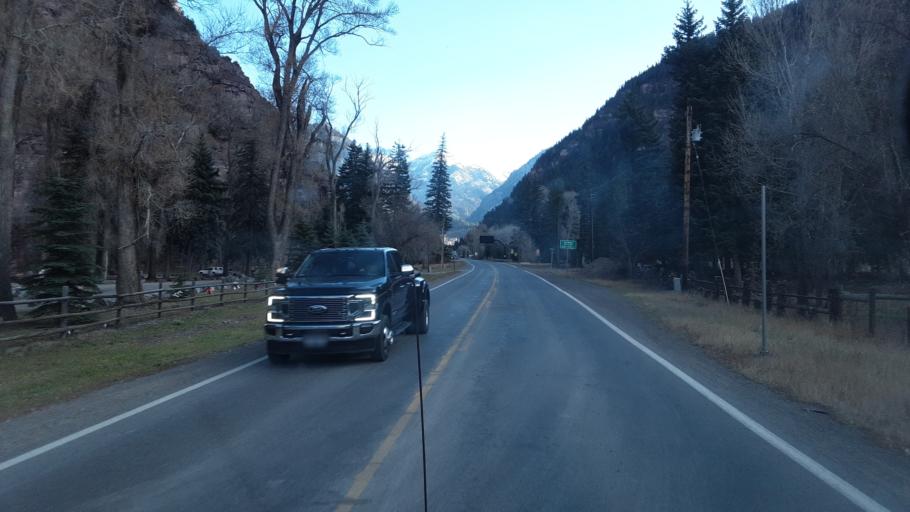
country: US
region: Colorado
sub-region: Ouray County
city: Ouray
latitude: 38.0449
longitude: -107.6819
